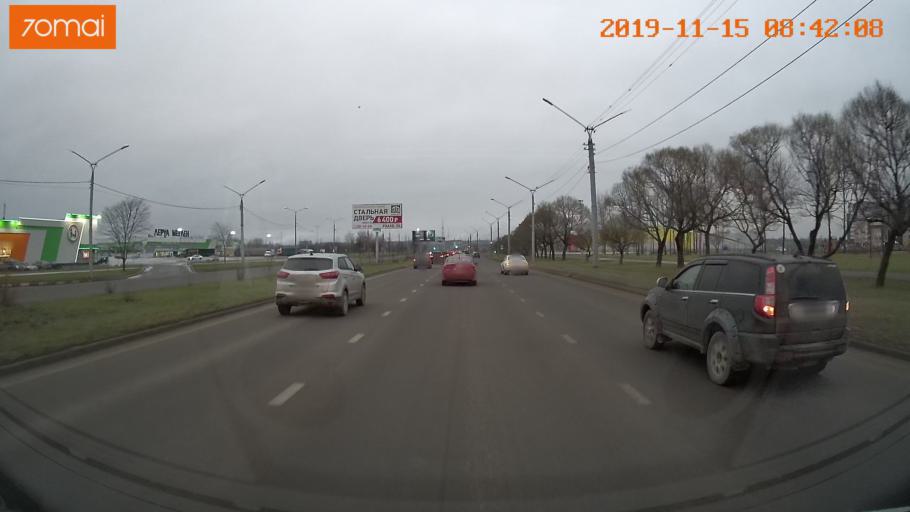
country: RU
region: Vologda
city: Cherepovets
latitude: 59.1007
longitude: 37.9096
